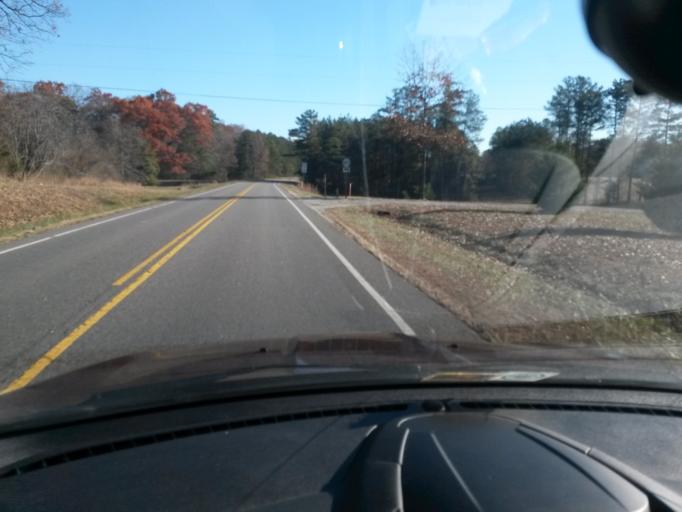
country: US
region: Virginia
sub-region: Charlotte County
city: Charlotte Court House
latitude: 37.0468
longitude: -78.5150
